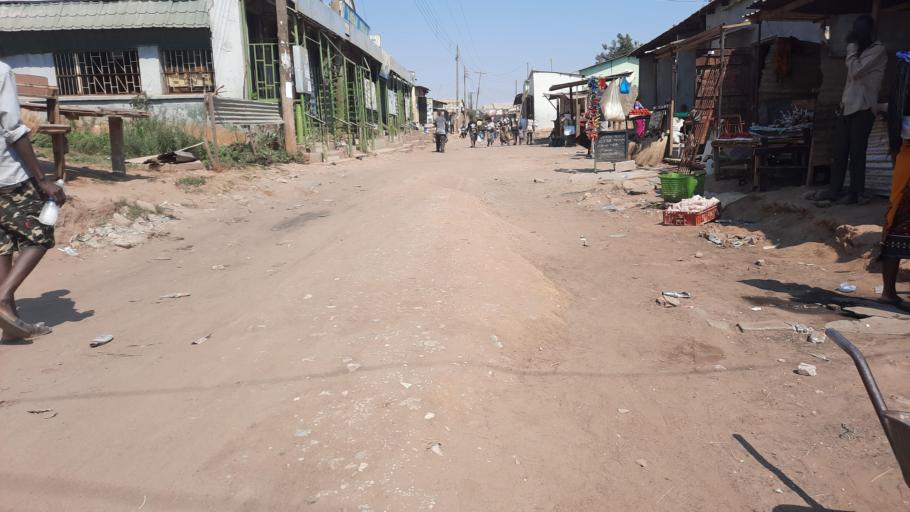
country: ZM
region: Lusaka
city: Lusaka
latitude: -15.3967
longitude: 28.3806
